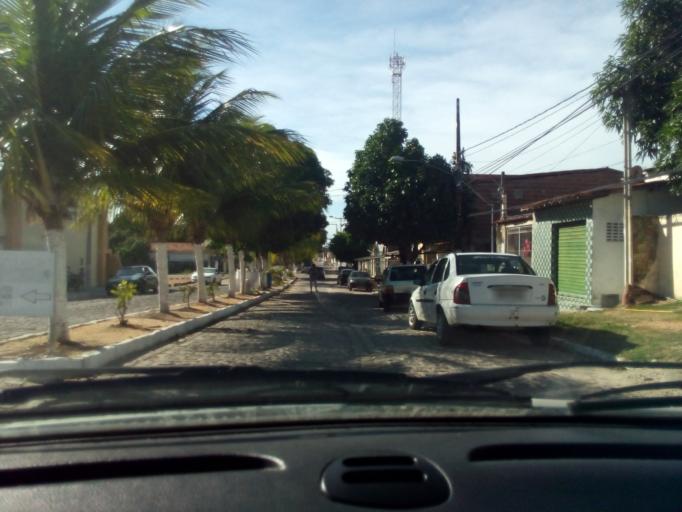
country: BR
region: Rio Grande do Norte
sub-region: Parnamirim
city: Parnamirim
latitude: -5.8842
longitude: -35.2054
